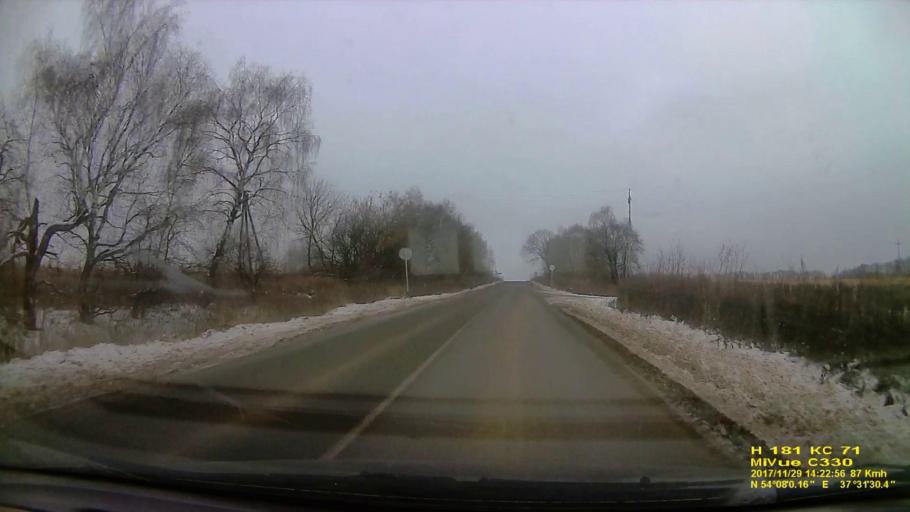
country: RU
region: Tula
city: Kosaya Gora
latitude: 54.1332
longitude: 37.5253
